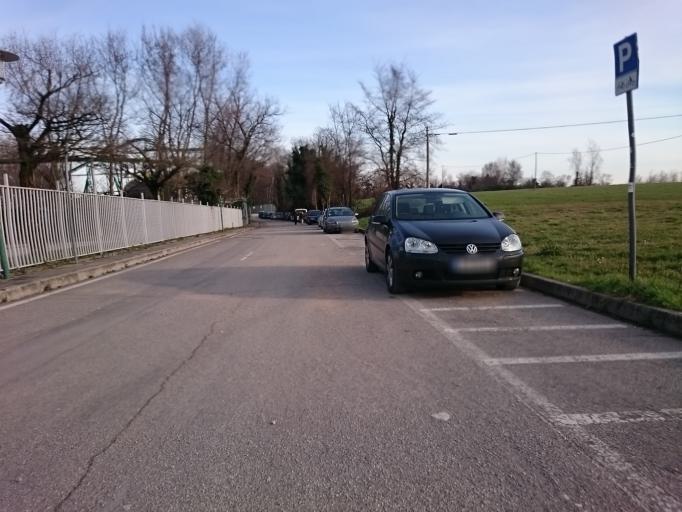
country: IT
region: Veneto
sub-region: Provincia di Verona
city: Peschiera del Garda
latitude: 45.4577
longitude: 10.7048
